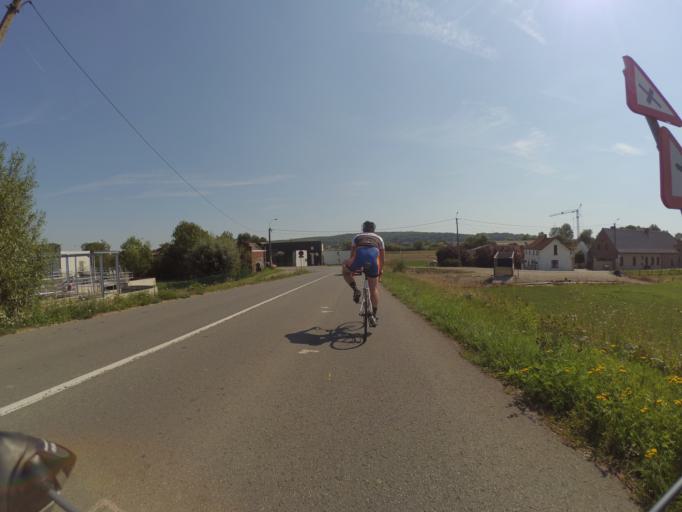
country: BE
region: Flanders
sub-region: Provincie West-Vlaanderen
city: Avelgem
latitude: 50.7737
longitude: 3.4732
